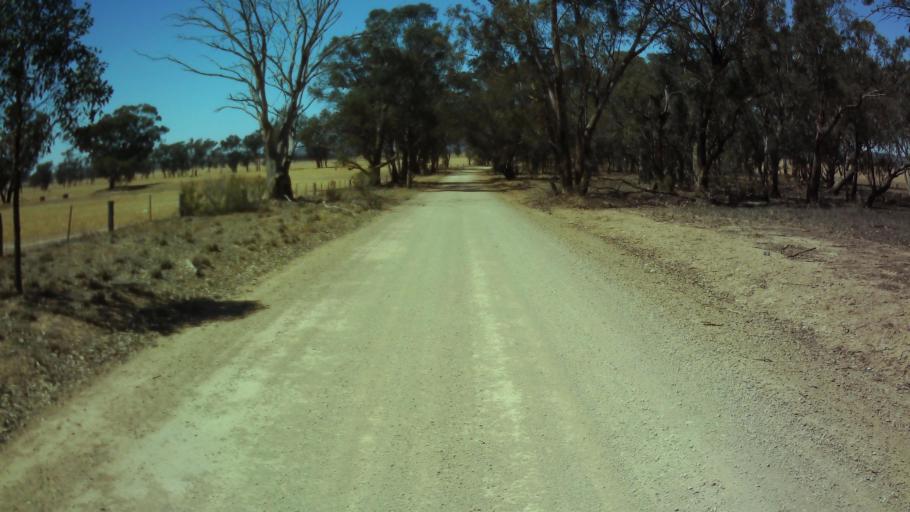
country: AU
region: New South Wales
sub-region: Weddin
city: Grenfell
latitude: -33.8869
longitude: 148.0877
